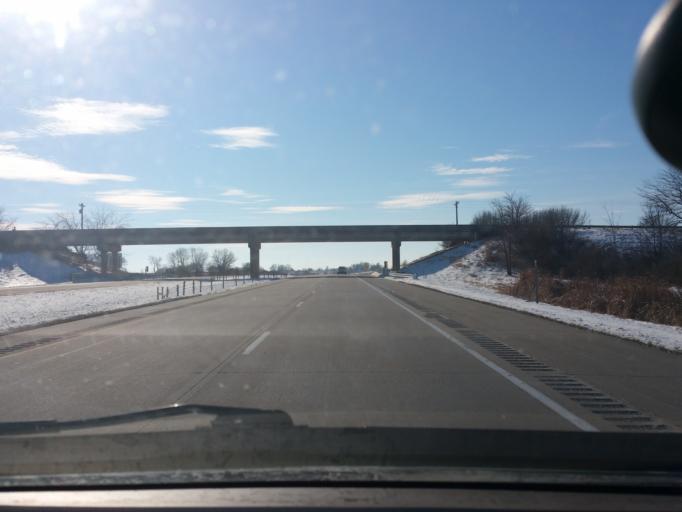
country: US
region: Iowa
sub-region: Clarke County
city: Osceola
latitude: 40.9730
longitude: -93.7977
